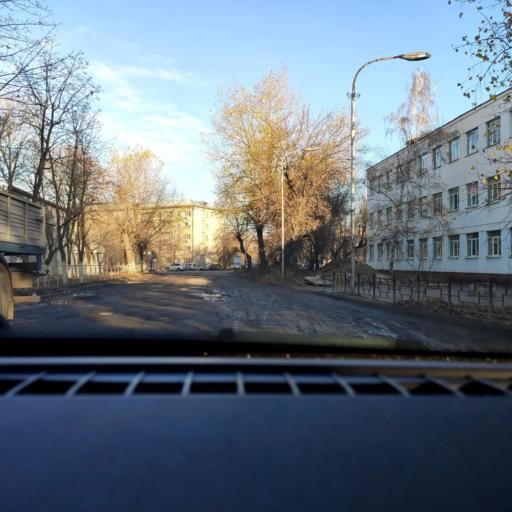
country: RU
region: Voronezj
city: Voronezh
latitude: 51.6347
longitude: 39.2503
